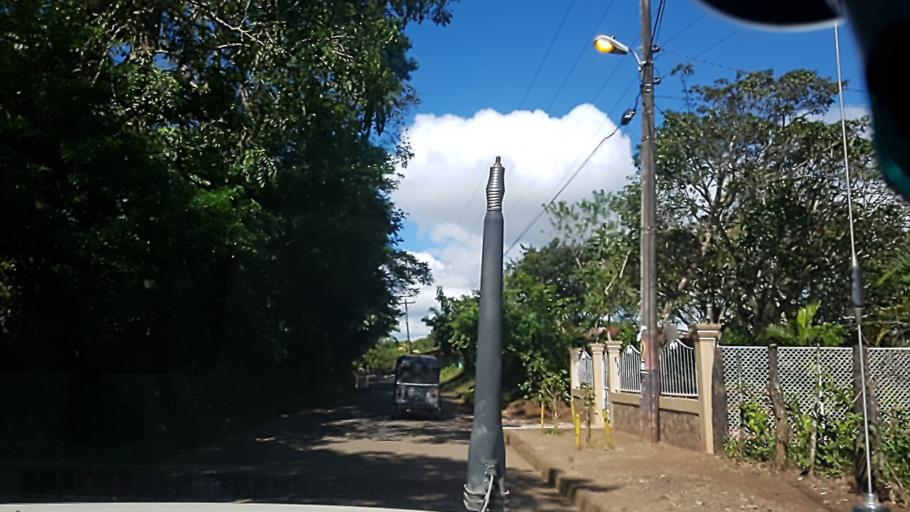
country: NI
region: Carazo
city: La Paz de Oriente
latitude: 11.8324
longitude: -86.1596
